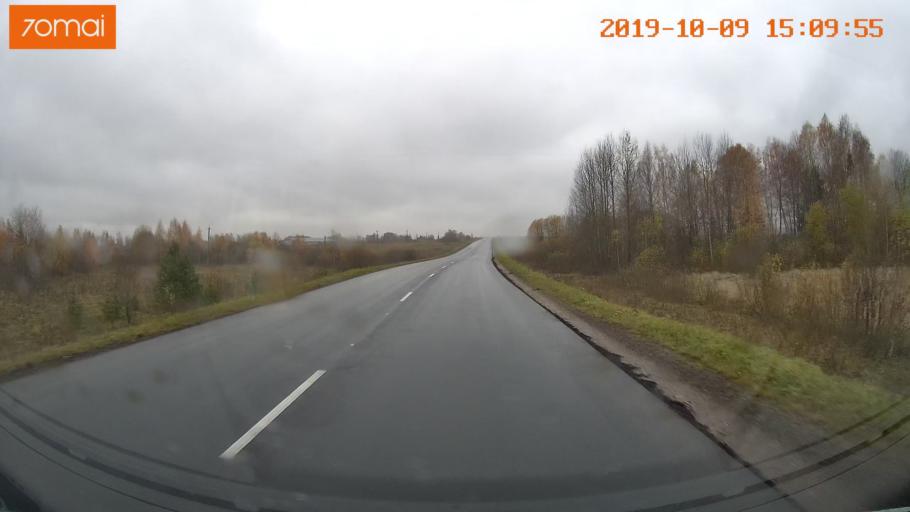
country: RU
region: Kostroma
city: Susanino
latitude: 58.1847
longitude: 41.6473
